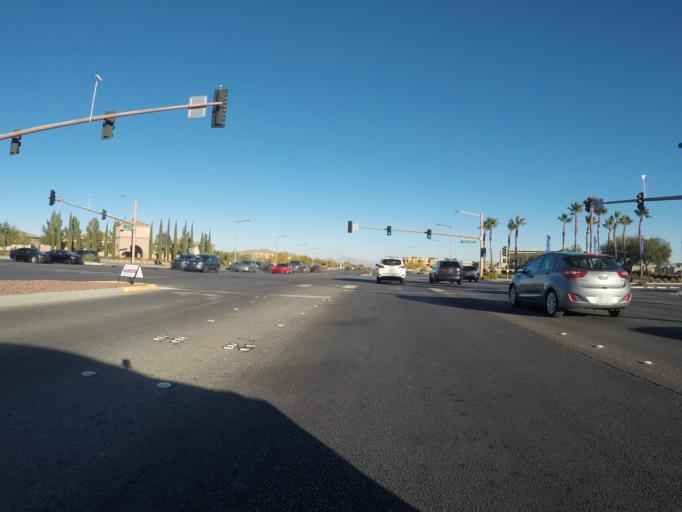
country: US
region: Nevada
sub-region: Clark County
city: Summerlin South
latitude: 36.1589
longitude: -115.3448
